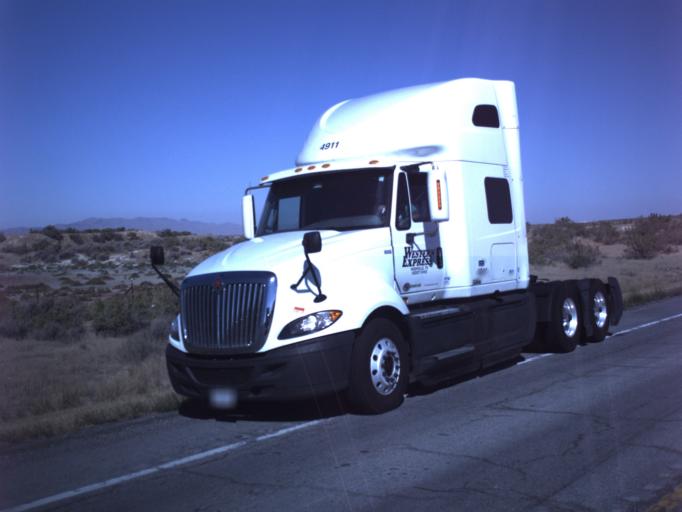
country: US
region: Utah
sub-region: Tooele County
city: Grantsville
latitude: 40.7044
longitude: -112.5300
